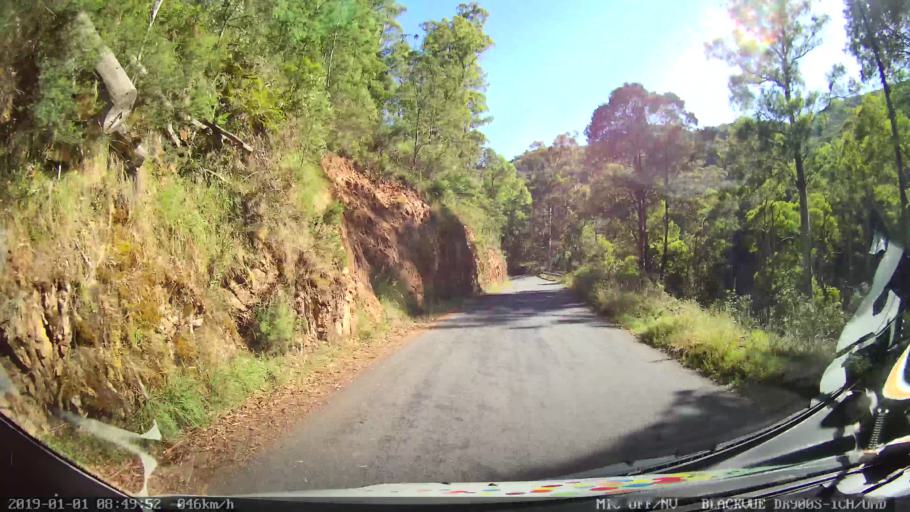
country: AU
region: New South Wales
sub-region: Snowy River
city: Jindabyne
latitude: -36.2798
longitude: 148.2014
